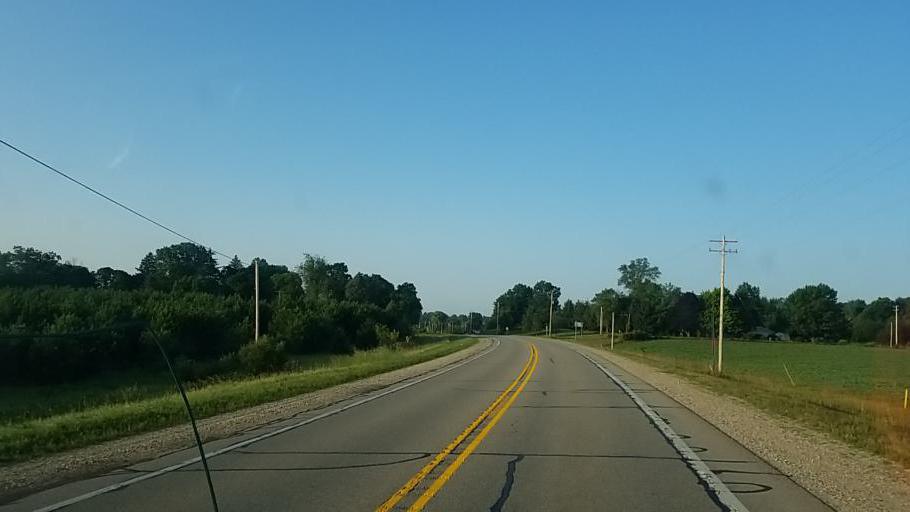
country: US
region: Michigan
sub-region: Montcalm County
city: Edmore
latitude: 43.4460
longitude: -85.1486
